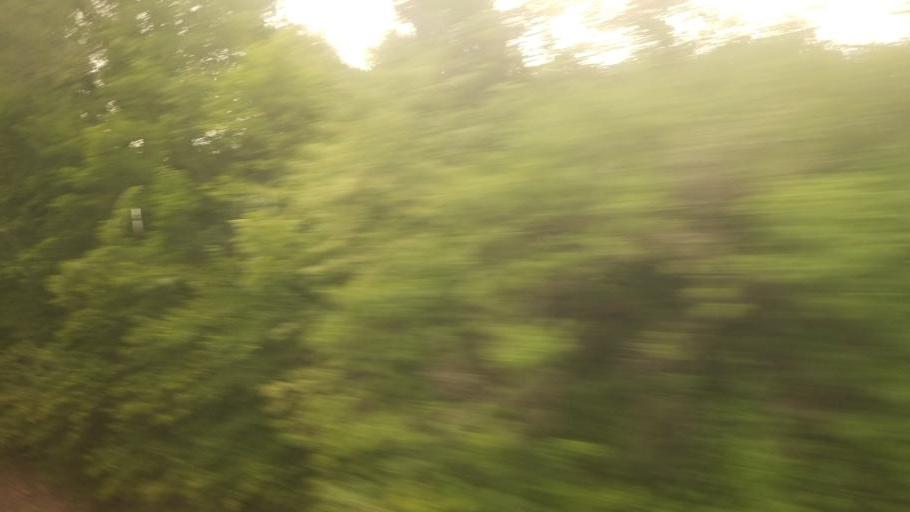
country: US
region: Kansas
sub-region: Shawnee County
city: Topeka
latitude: 39.0271
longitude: -95.6745
